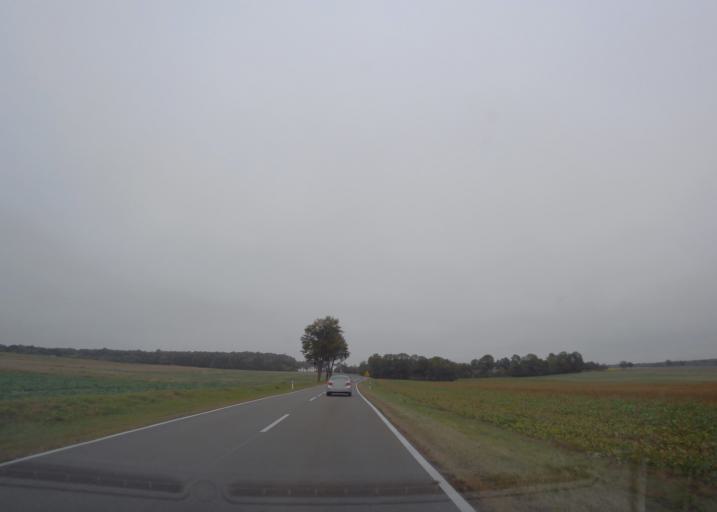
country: PL
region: Lublin Voivodeship
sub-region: Powiat chelmski
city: Rejowiec
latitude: 51.0554
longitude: 23.2673
